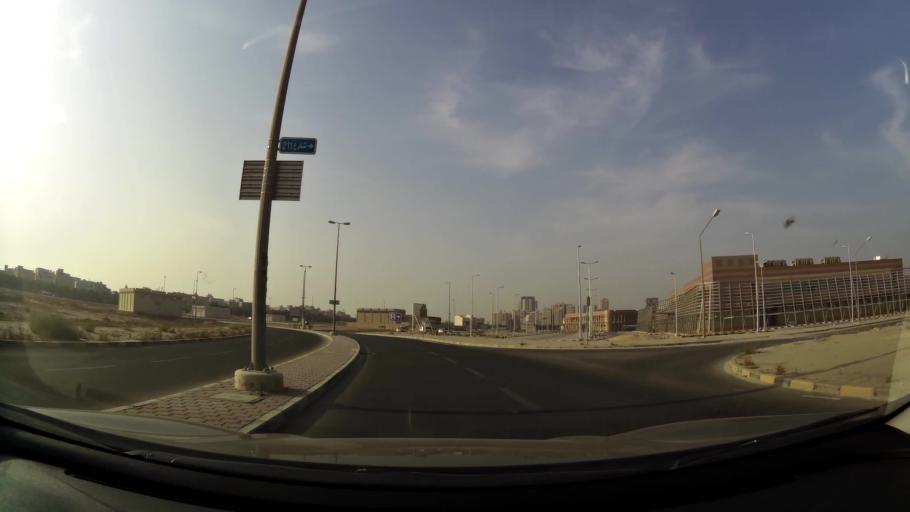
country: KW
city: Al Funaytis
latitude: 29.2407
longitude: 48.0867
